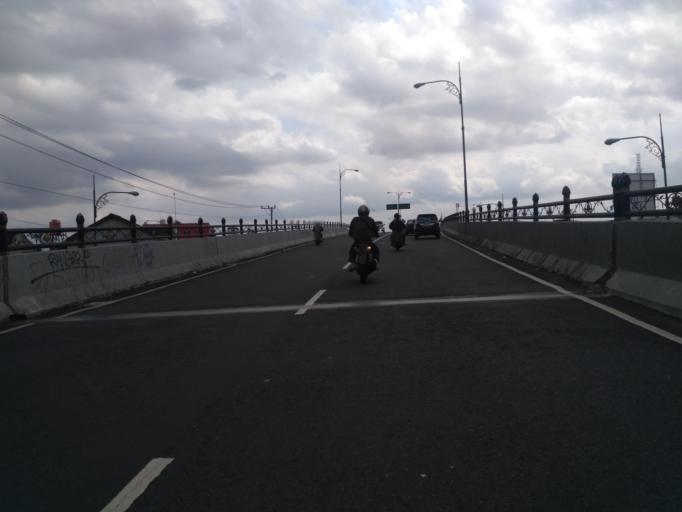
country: ID
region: Daerah Istimewa Yogyakarta
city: Melati
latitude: -7.7499
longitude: 110.3639
